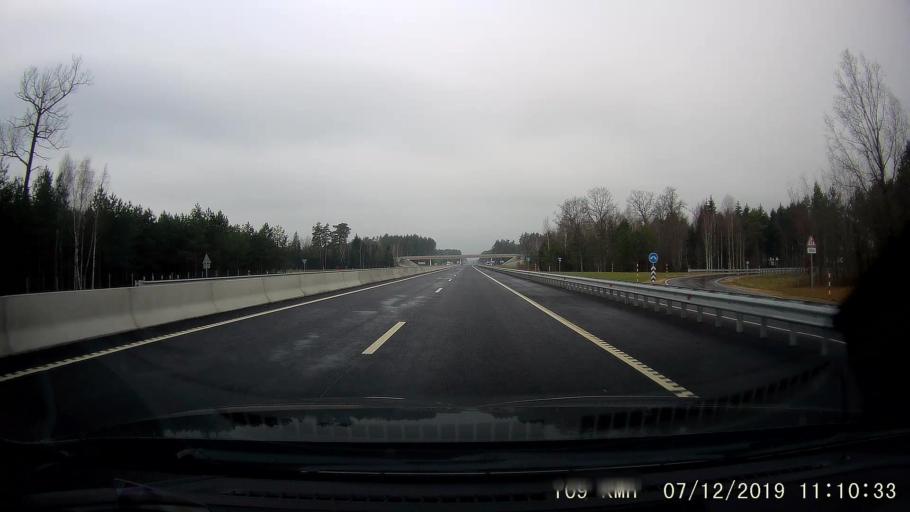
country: BY
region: Grodnenskaya
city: Iwye
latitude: 53.8821
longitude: 25.7453
